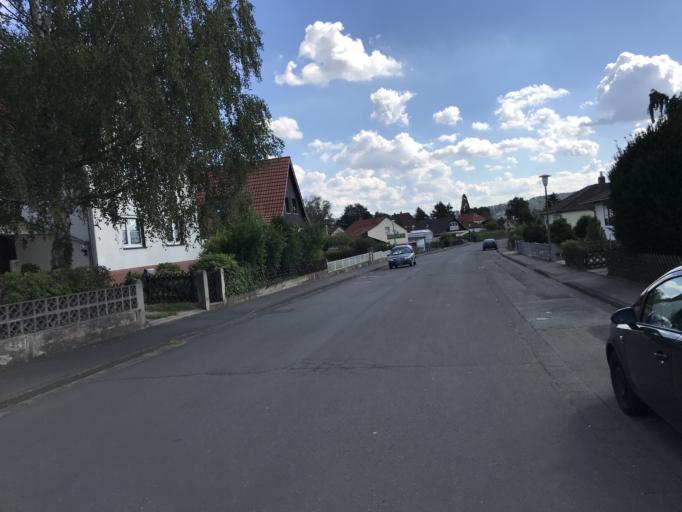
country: DE
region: Hesse
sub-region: Regierungsbezirk Kassel
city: Bad Sooden-Allendorf
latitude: 51.2735
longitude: 9.9795
